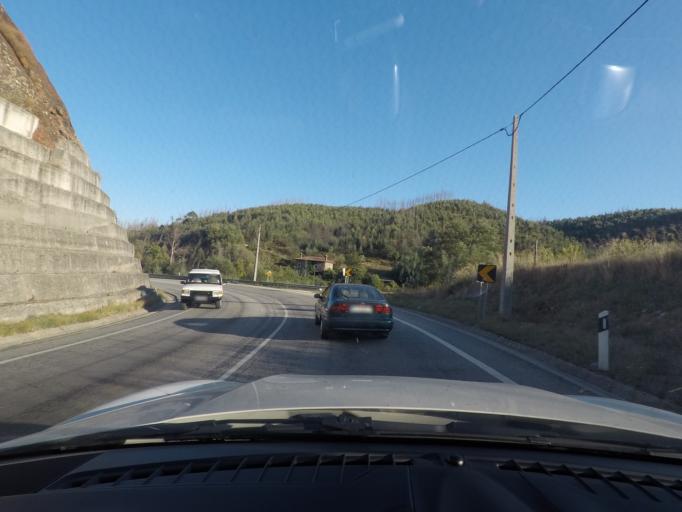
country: PT
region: Coimbra
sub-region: Vila Nova de Poiares
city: Poiares
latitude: 40.1715
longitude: -8.3028
